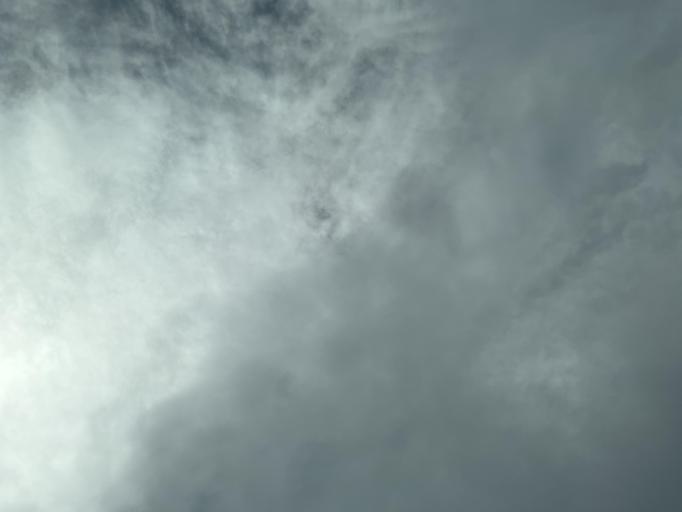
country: SV
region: La Union
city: La Union
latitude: 13.3738
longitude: -87.9093
